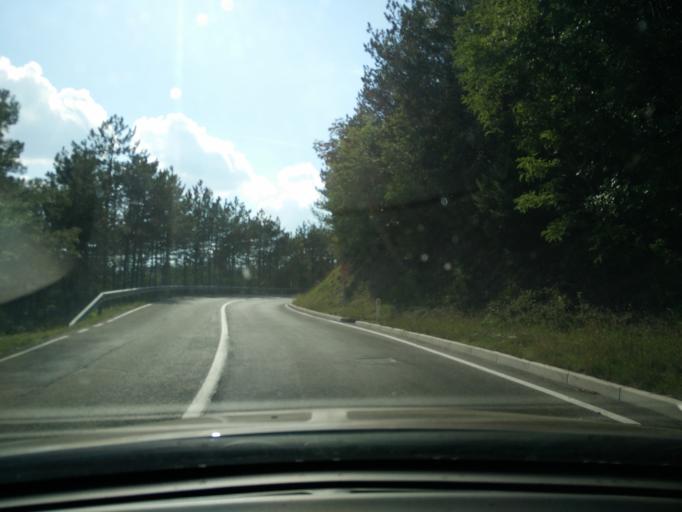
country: HR
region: Istarska
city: Buzet
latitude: 45.4593
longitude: 13.9050
